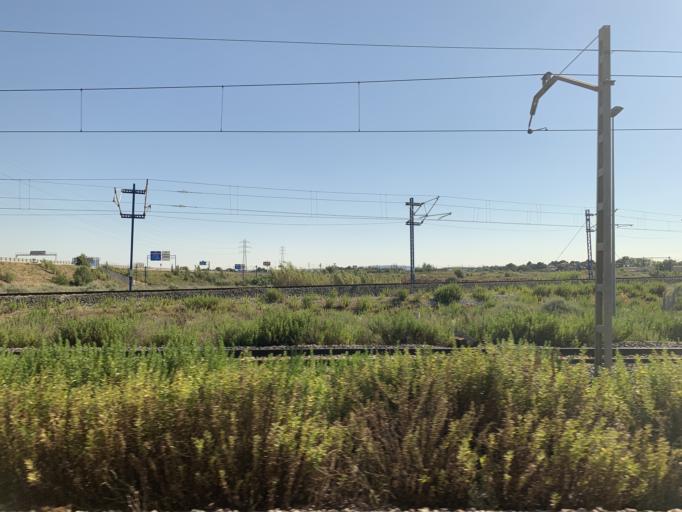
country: ES
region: Aragon
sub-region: Provincia de Zaragoza
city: Oliver-Valdefierro, Oliver, Valdefierro
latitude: 41.6715
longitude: -0.9338
